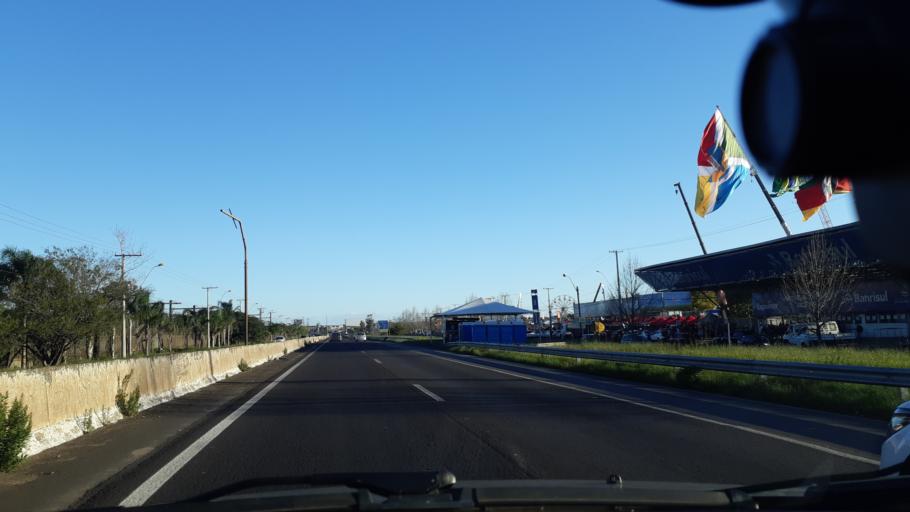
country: BR
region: Rio Grande do Sul
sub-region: Esteio
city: Esteio
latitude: -29.8537
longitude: -51.1800
